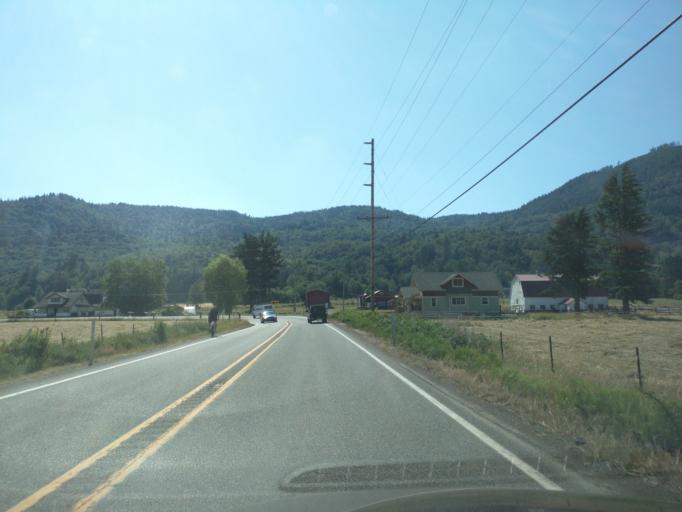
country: US
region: Washington
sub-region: Whatcom County
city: Peaceful Valley
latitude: 48.9051
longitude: -122.1417
